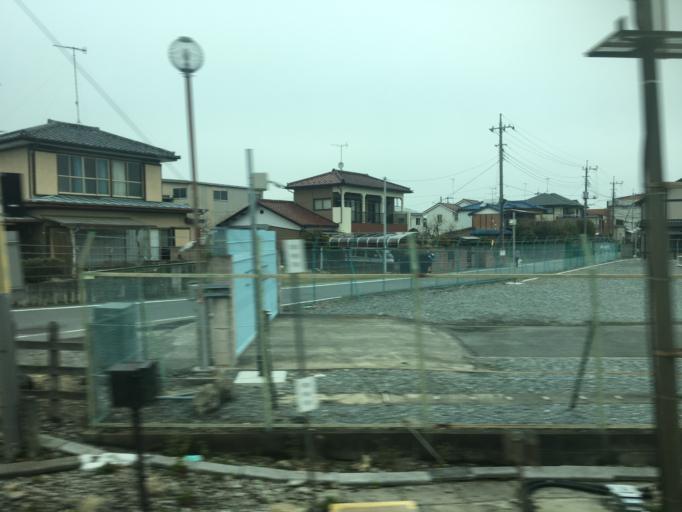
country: JP
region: Saitama
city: Kumagaya
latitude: 36.1679
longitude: 139.3433
